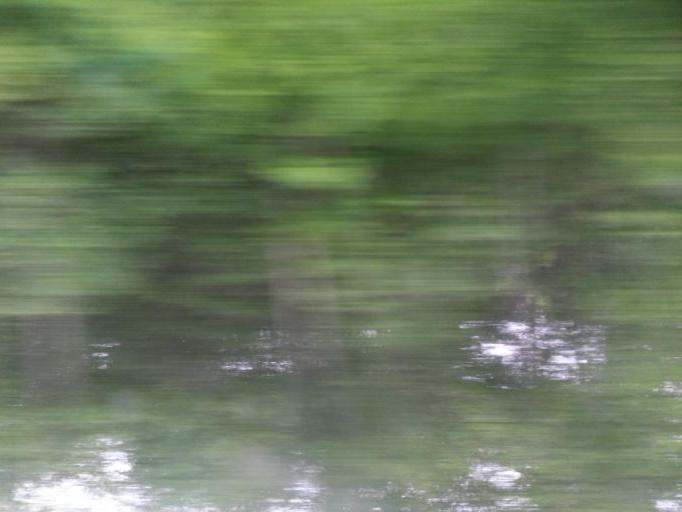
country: NO
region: Sor-Trondelag
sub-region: Melhus
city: Melhus
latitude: 63.3439
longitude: 10.3498
